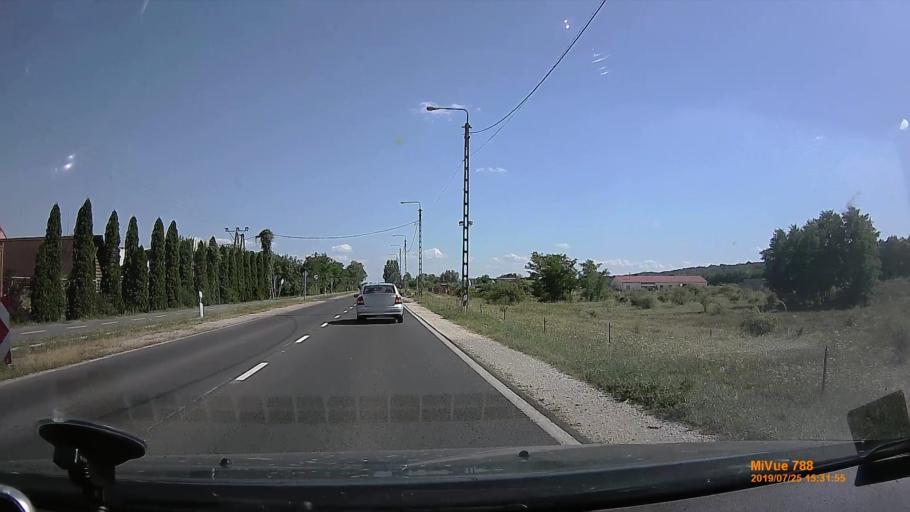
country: HU
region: Borsod-Abauj-Zemplen
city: Malyi
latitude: 48.0102
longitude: 20.8261
